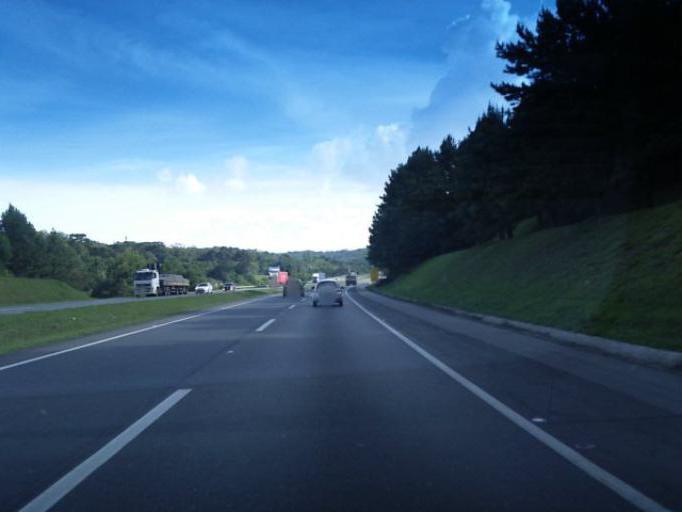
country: BR
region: Parana
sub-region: Quatro Barras
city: Quatro Barras
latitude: -25.3561
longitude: -49.0410
